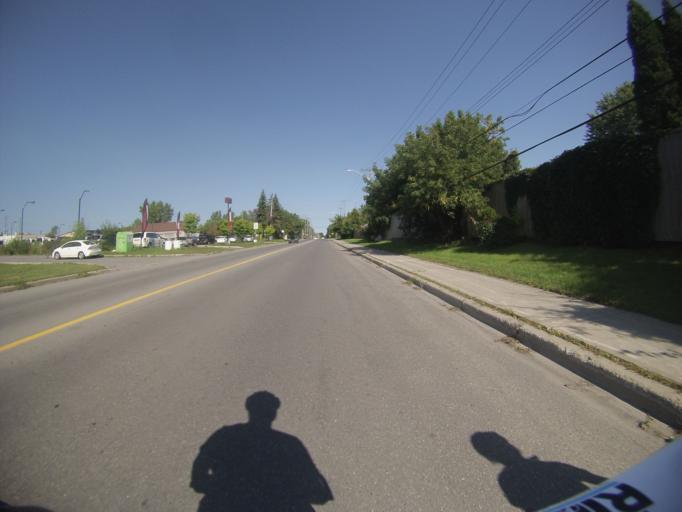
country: CA
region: Ontario
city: Ottawa
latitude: 45.3631
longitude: -75.6500
